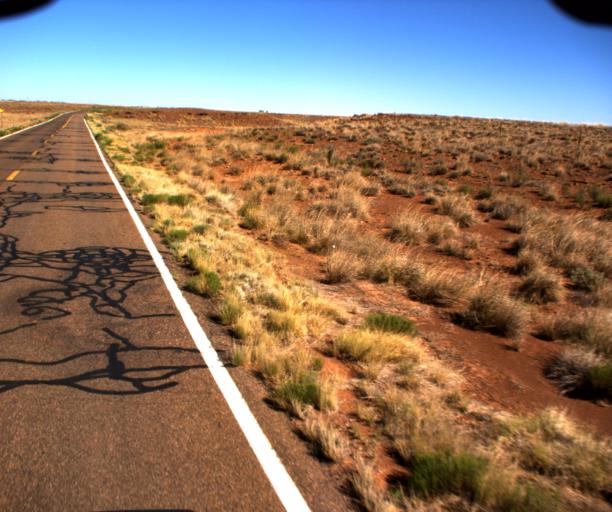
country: US
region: Arizona
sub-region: Coconino County
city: LeChee
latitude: 35.2602
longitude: -110.9671
